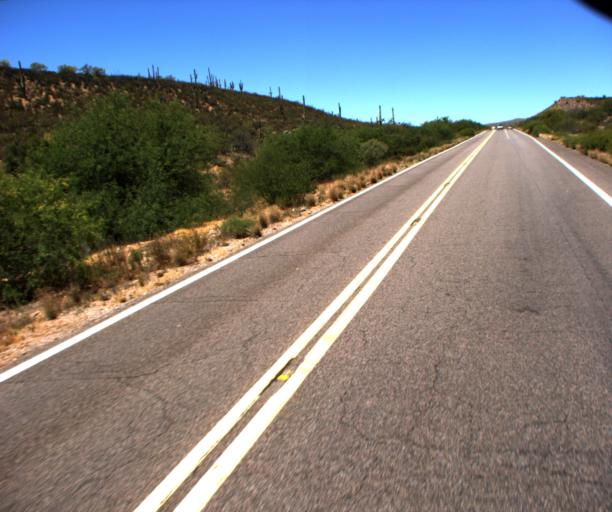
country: US
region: Arizona
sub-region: Pinal County
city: Kearny
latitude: 33.1296
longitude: -110.7793
